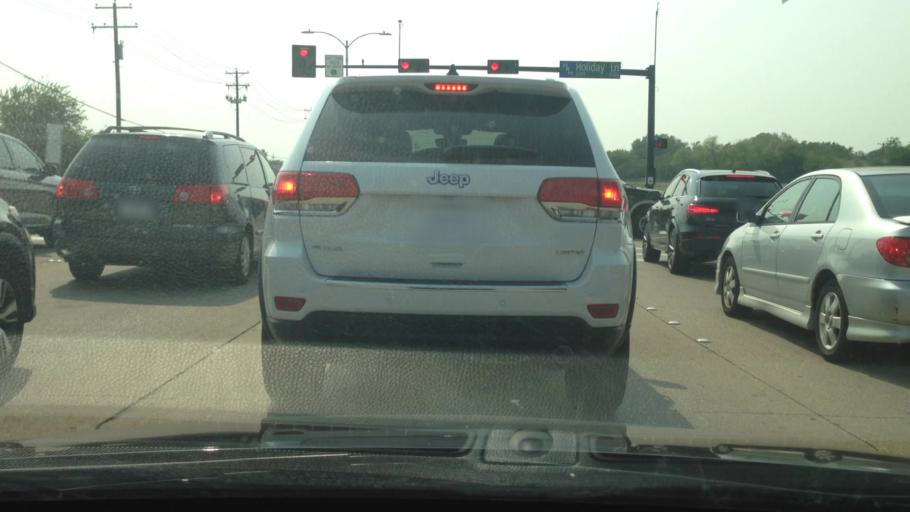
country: US
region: Texas
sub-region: Tarrant County
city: North Richland Hills
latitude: 32.8602
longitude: -97.2177
